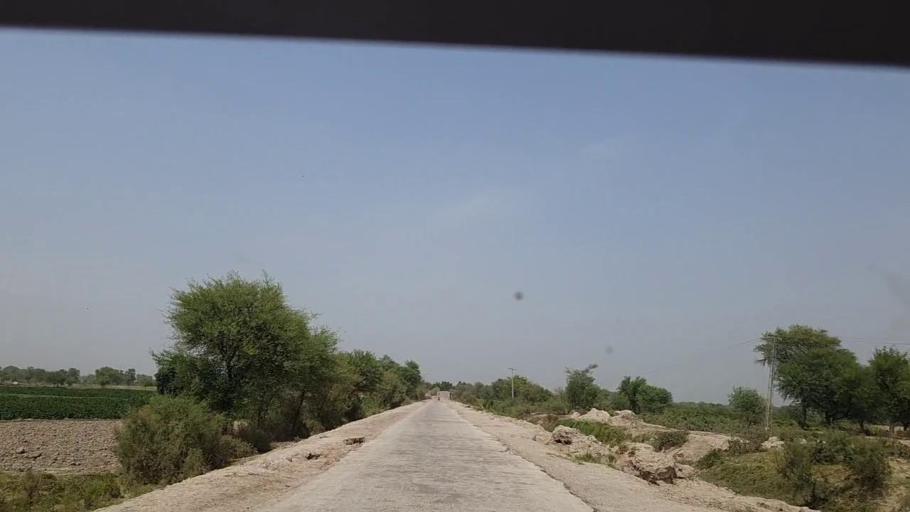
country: PK
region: Sindh
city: Khairpur Nathan Shah
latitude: 27.0782
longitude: 67.6551
